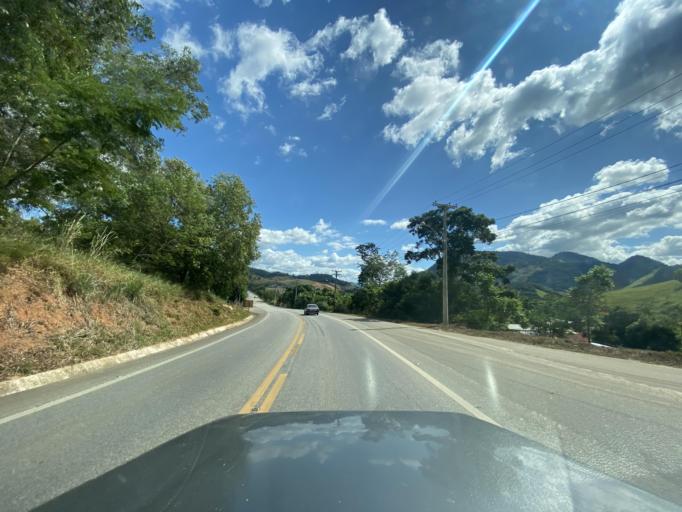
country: BR
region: Espirito Santo
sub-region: Jeronimo Monteiro
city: Jeronimo Monteiro
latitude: -20.7637
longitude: -41.4478
